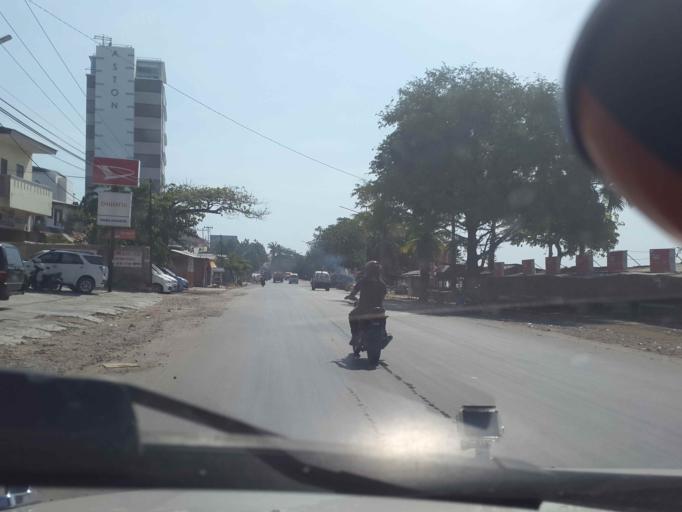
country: ID
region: East Nusa Tenggara
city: Kelapalima
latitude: -10.1443
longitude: 123.6181
